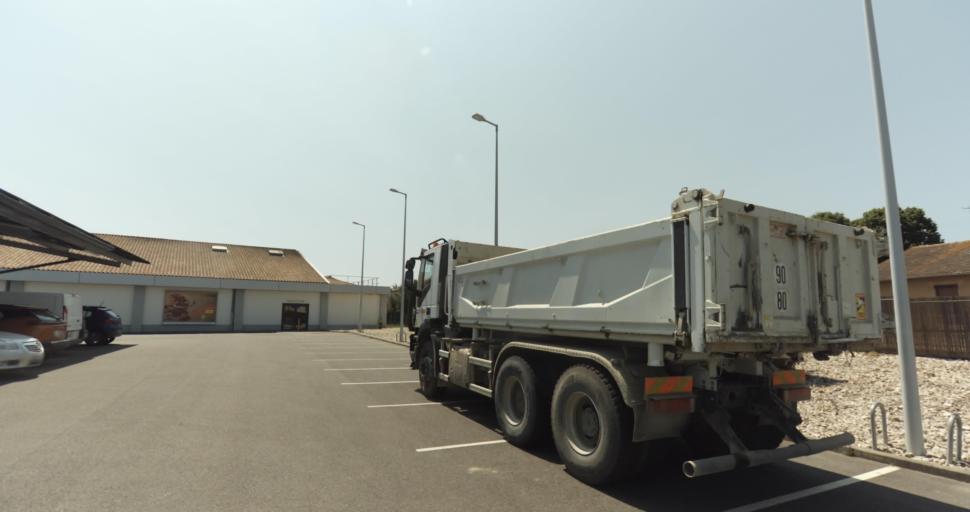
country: FR
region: Midi-Pyrenees
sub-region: Departement de la Haute-Garonne
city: Leguevin
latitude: 43.6005
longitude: 1.2474
